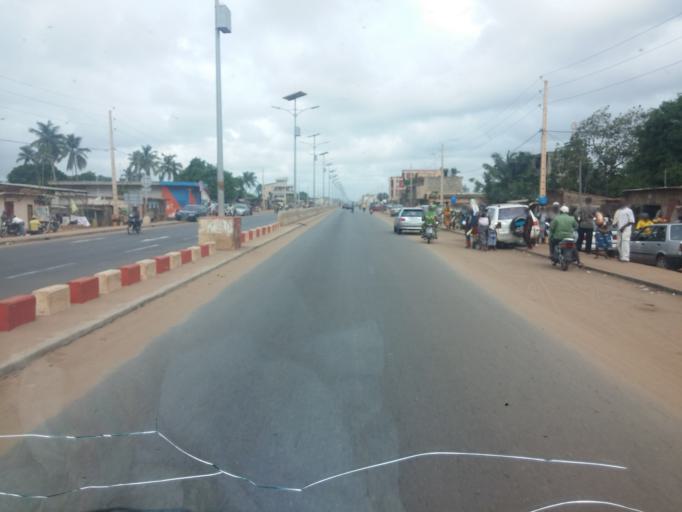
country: BJ
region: Atlantique
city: Hevie
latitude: 6.3880
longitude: 2.2714
